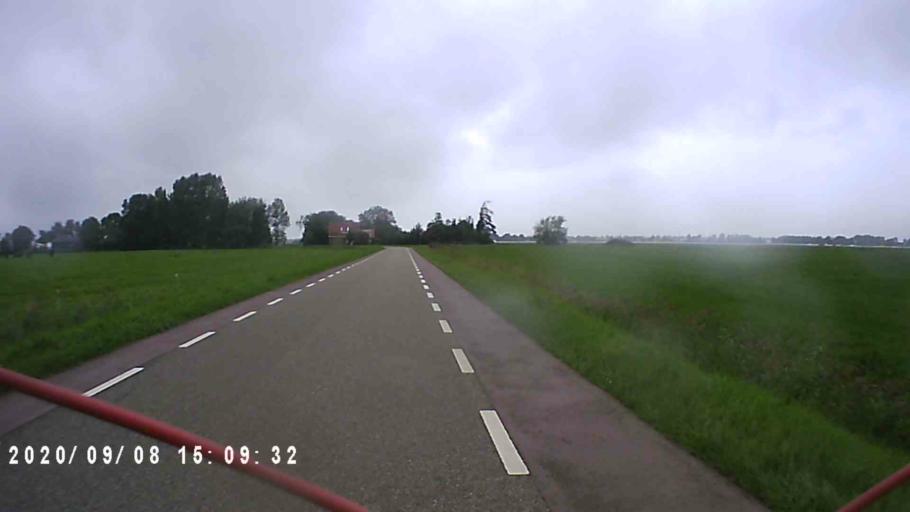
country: NL
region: Groningen
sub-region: Gemeente Slochteren
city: Slochteren
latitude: 53.2733
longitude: 6.7271
